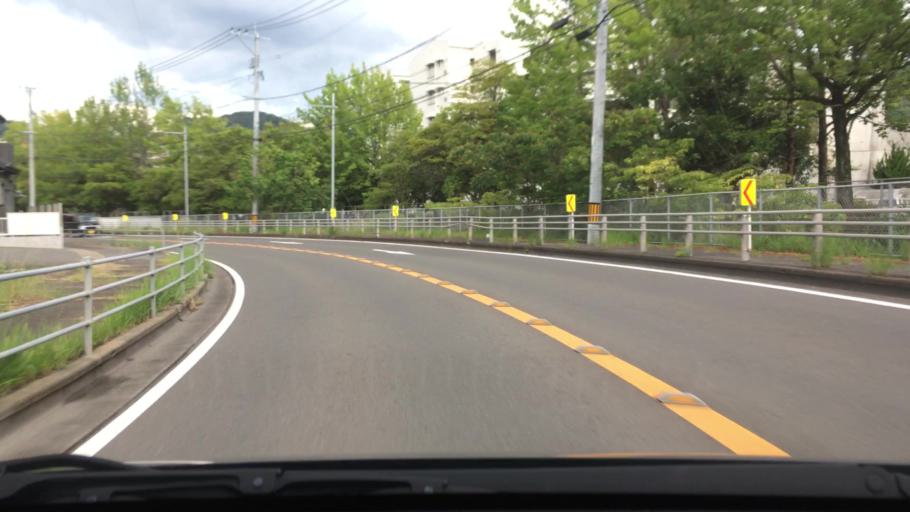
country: JP
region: Nagasaki
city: Togitsu
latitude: 32.8256
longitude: 129.7745
